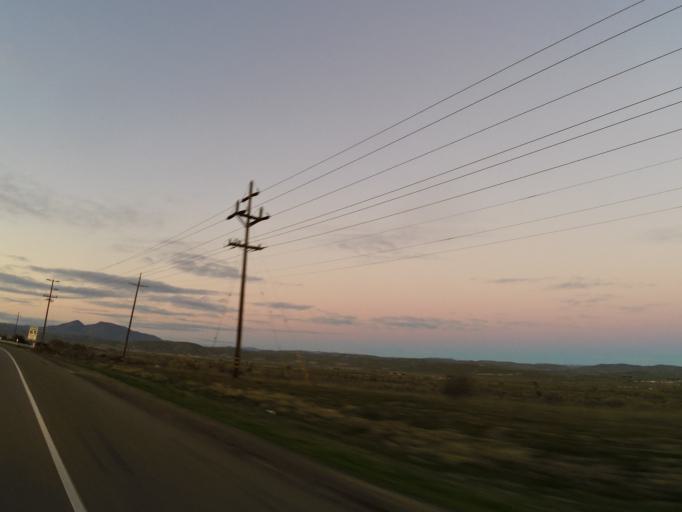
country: US
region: California
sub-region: Monterey County
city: King City
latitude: 36.2681
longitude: -121.1806
